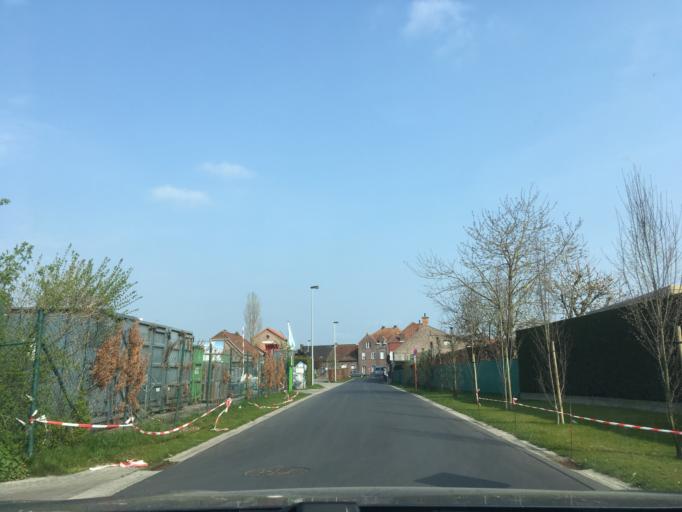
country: BE
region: Flanders
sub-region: Provincie West-Vlaanderen
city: Ardooie
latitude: 50.9897
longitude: 3.2017
